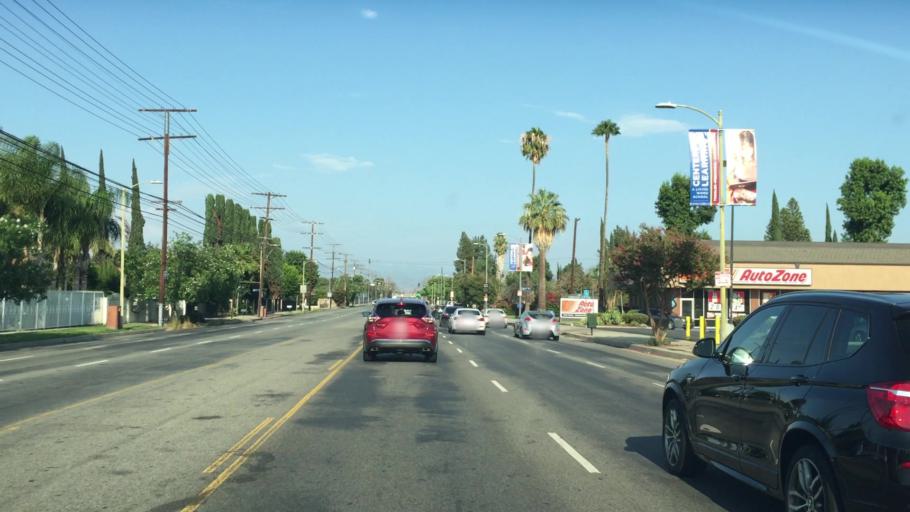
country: US
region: California
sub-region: Los Angeles County
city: Northridge
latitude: 34.2356
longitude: -118.4838
